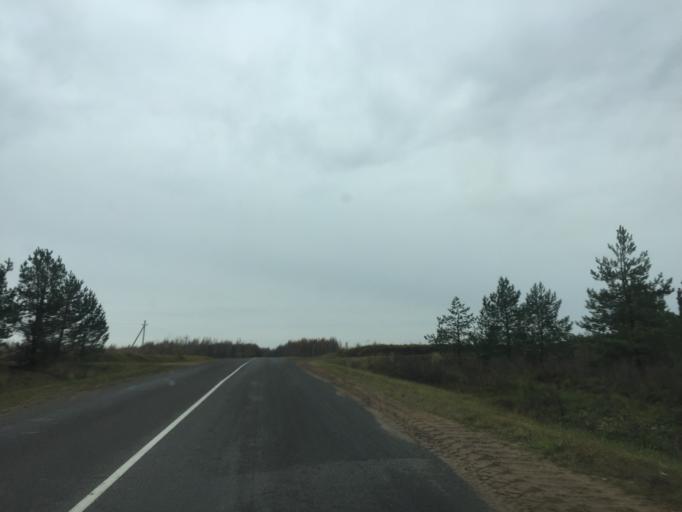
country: BY
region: Mogilev
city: Drybin
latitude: 54.1091
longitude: 31.1140
